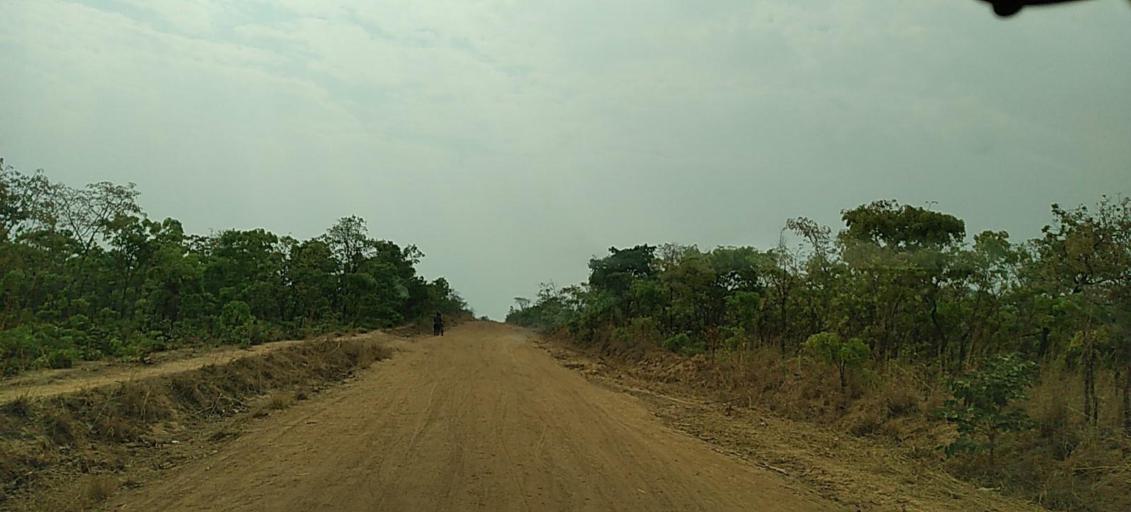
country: ZM
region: North-Western
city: Kabompo
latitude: -13.4163
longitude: 24.3914
